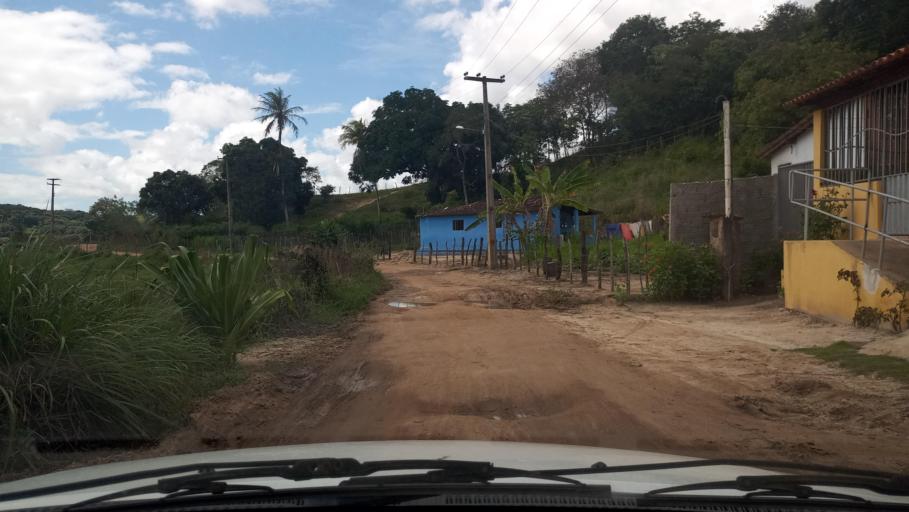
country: BR
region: Rio Grande do Norte
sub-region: Goianinha
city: Goianinha
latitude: -6.2613
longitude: -35.2520
